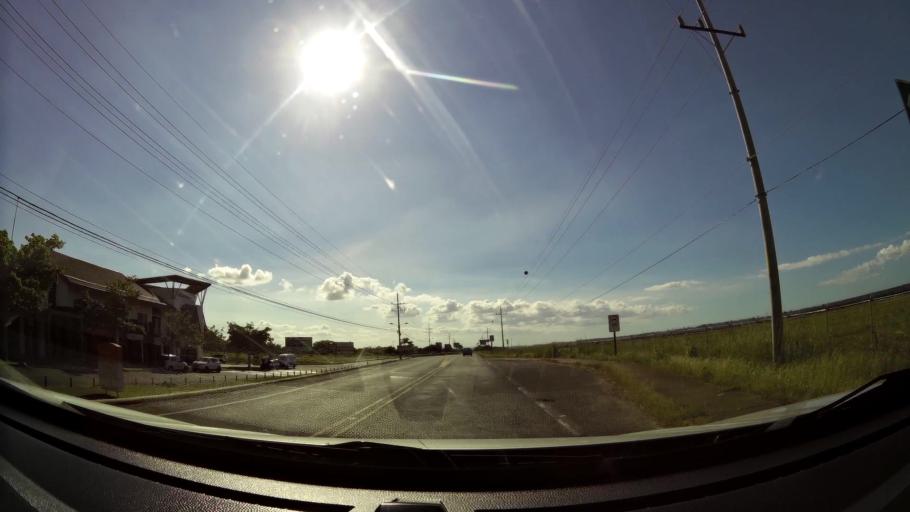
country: CR
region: Guanacaste
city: Liberia
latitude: 10.5942
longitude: -85.5339
